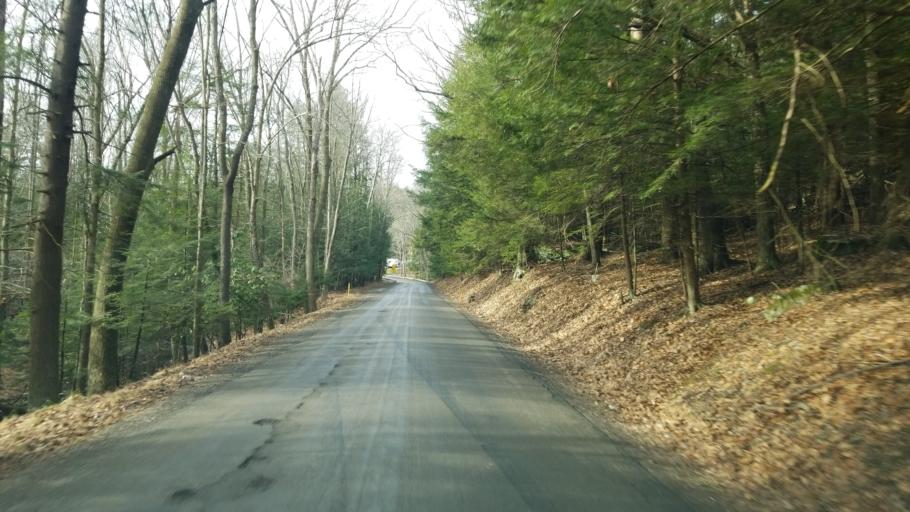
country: US
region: Pennsylvania
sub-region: Indiana County
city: Johnsonburg
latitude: 40.8259
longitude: -78.9740
